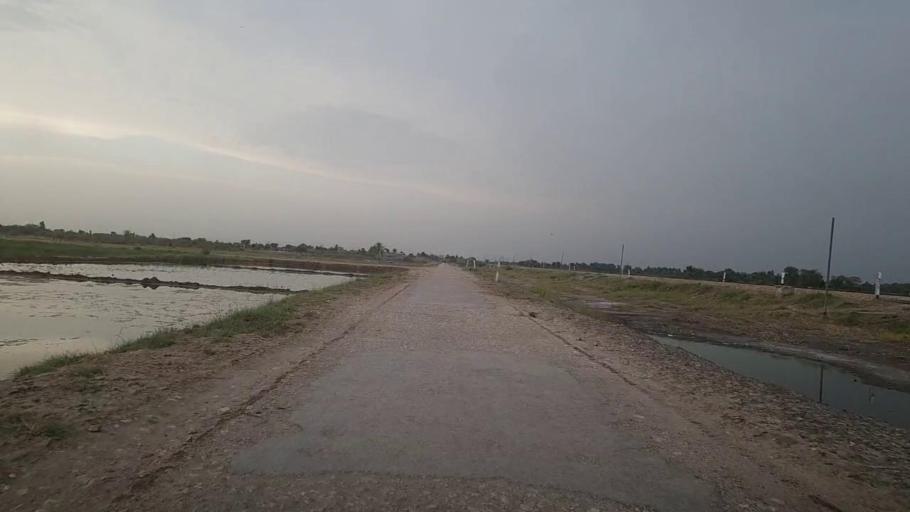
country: PK
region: Sindh
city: Karaundi
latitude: 26.9975
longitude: 68.3498
